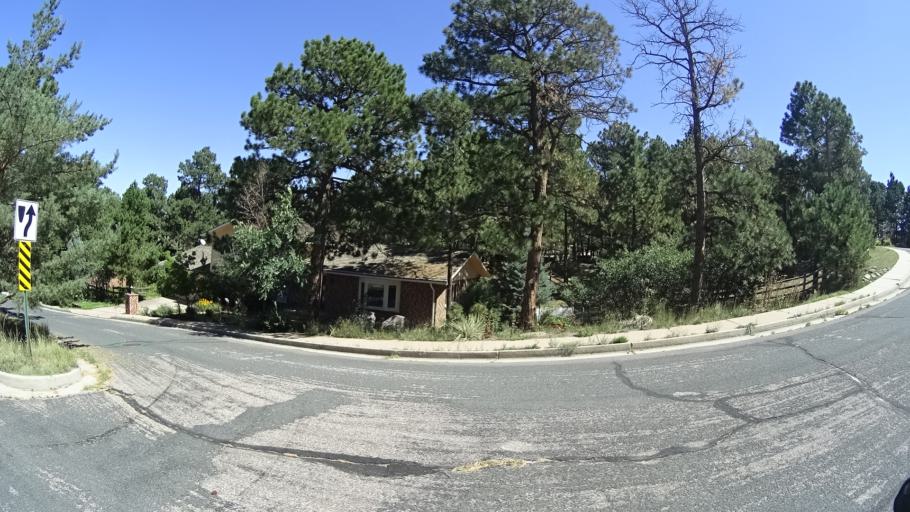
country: US
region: Colorado
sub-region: El Paso County
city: Colorado Springs
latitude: 38.9207
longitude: -104.7999
